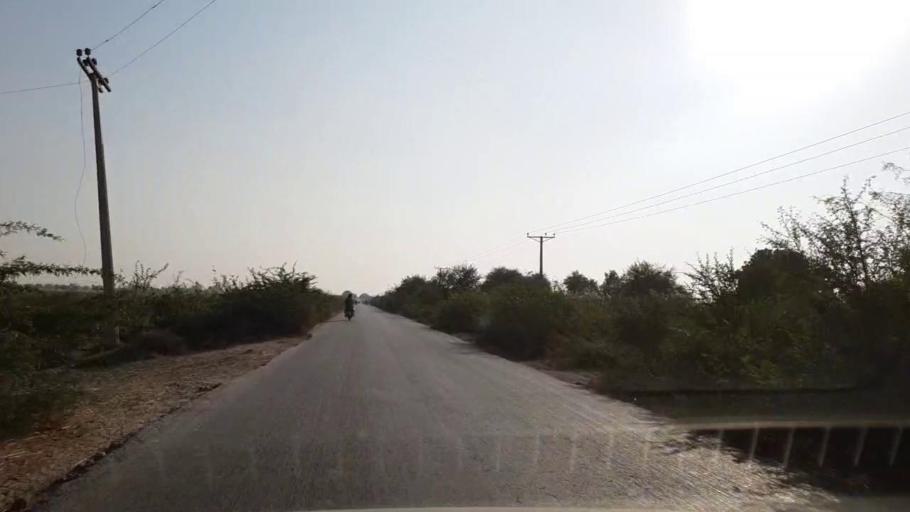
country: PK
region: Sindh
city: Bulri
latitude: 24.8837
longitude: 68.3421
